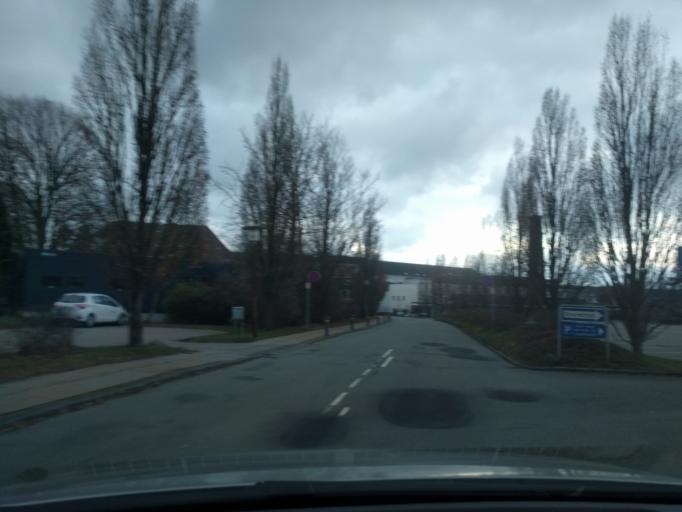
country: DK
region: South Denmark
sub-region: Nyborg Kommune
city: Nyborg
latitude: 55.3176
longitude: 10.7876
